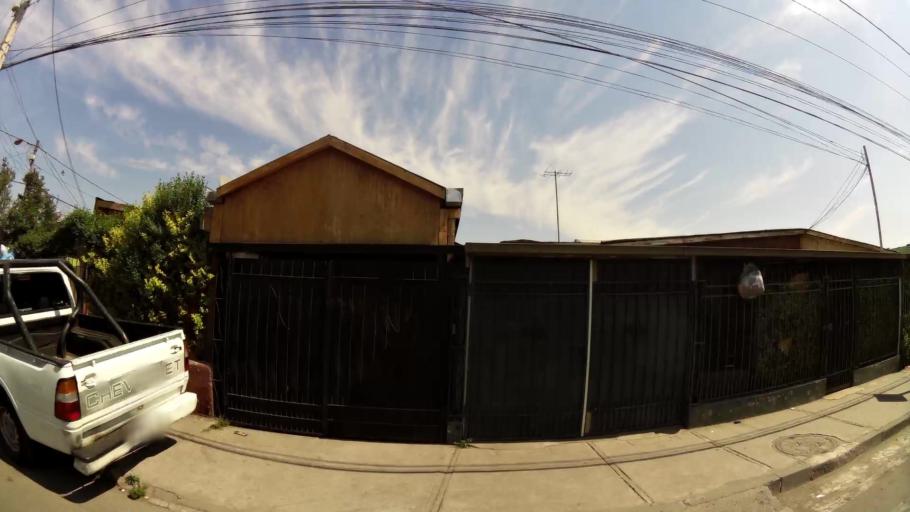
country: CL
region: Santiago Metropolitan
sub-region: Provincia de Santiago
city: La Pintana
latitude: -33.5517
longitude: -70.6412
